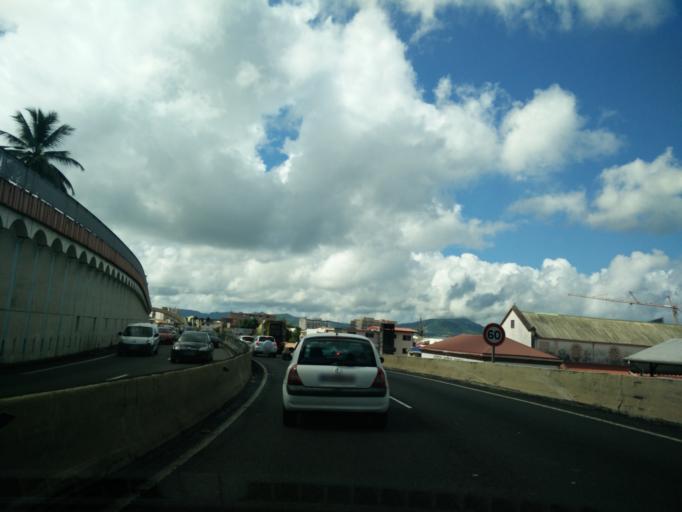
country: MQ
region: Martinique
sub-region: Martinique
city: Fort-de-France
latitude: 14.6128
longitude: -61.0705
